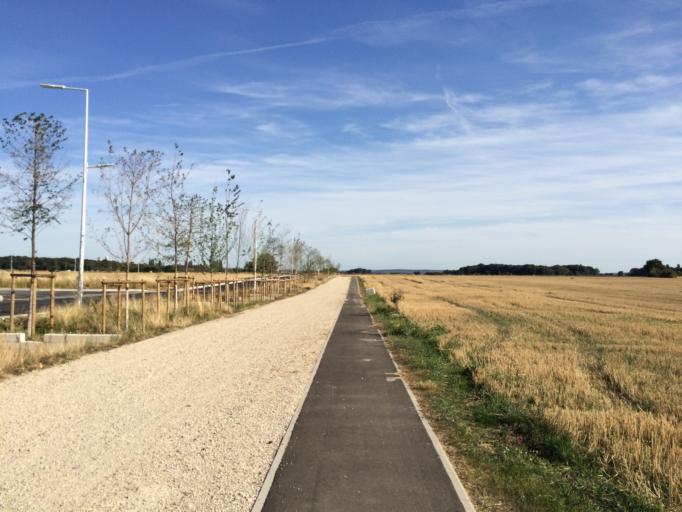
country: FR
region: Ile-de-France
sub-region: Departement de l'Essonne
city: Bretigny-sur-Orge
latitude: 48.5935
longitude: 2.3136
